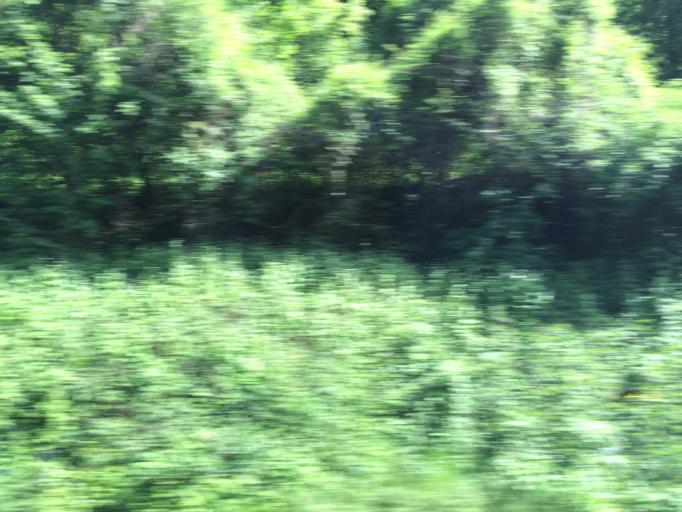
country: DE
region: Bavaria
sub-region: Regierungsbezirk Unterfranken
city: Rottendorf
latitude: 49.8034
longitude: 10.0514
